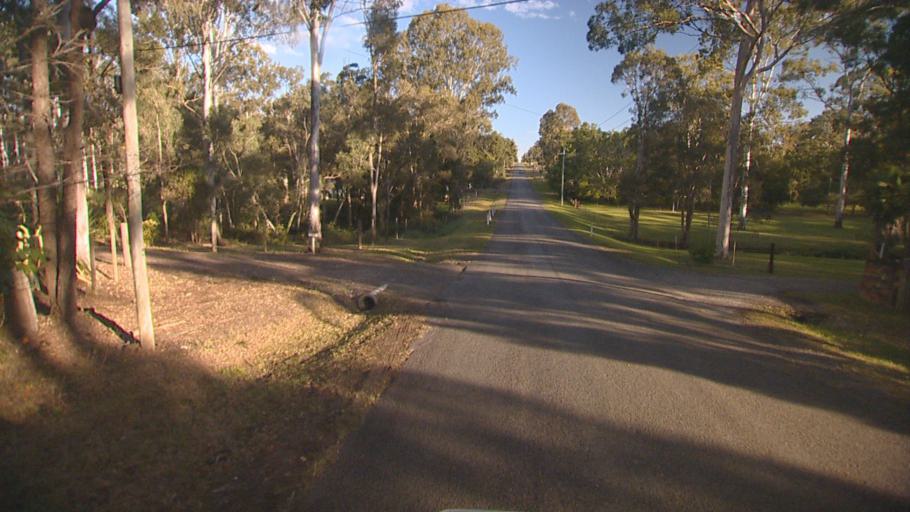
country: AU
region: Queensland
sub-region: Logan
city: Waterford West
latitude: -27.7218
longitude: 153.1539
